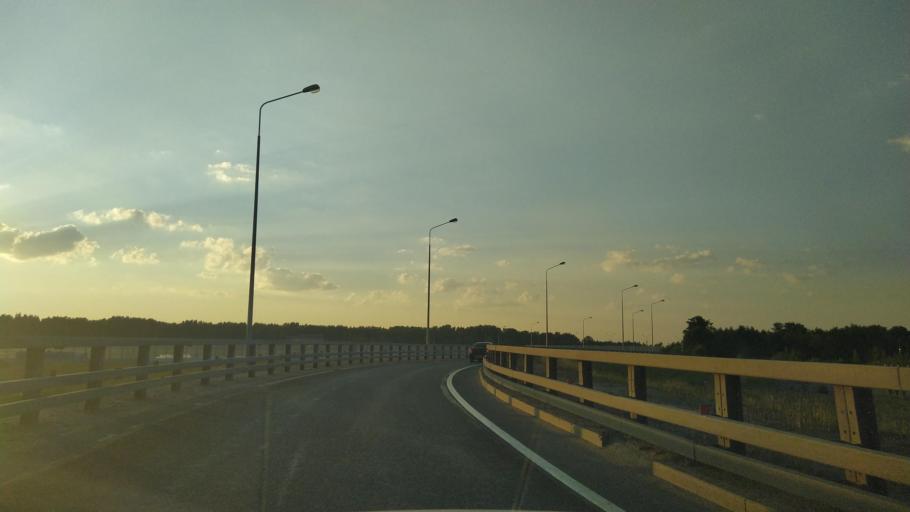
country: RU
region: St.-Petersburg
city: Kronshtadt
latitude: 60.0129
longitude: 29.7228
